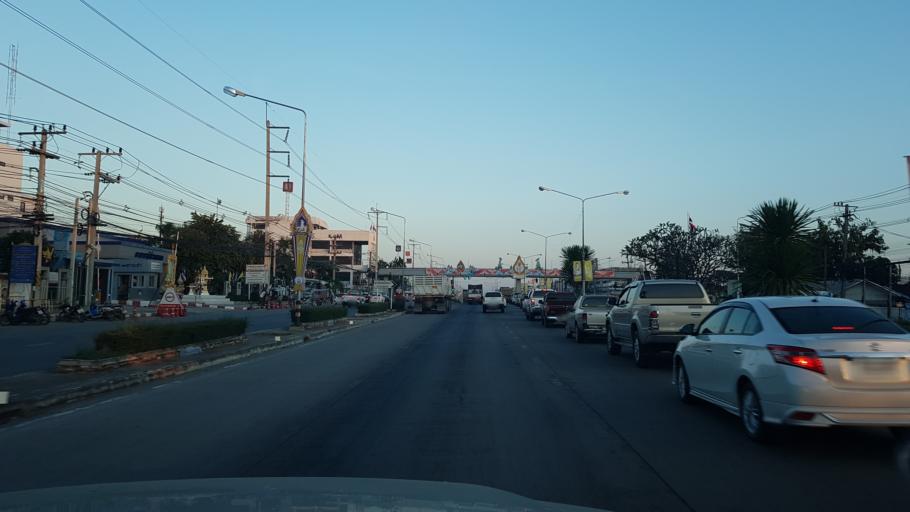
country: TH
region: Khon Kaen
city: Chum Phae
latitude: 16.5456
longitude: 102.0986
